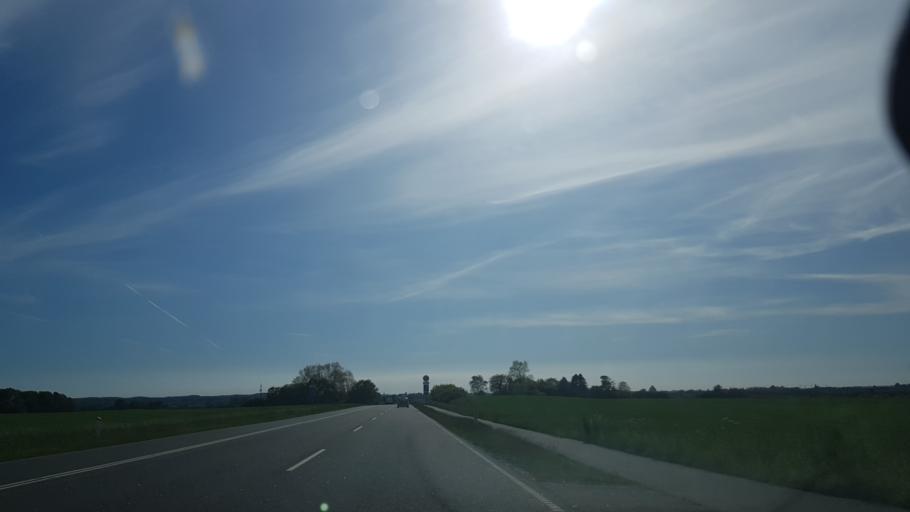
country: DK
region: Zealand
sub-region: Soro Kommune
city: Soro
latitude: 55.4325
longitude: 11.4820
